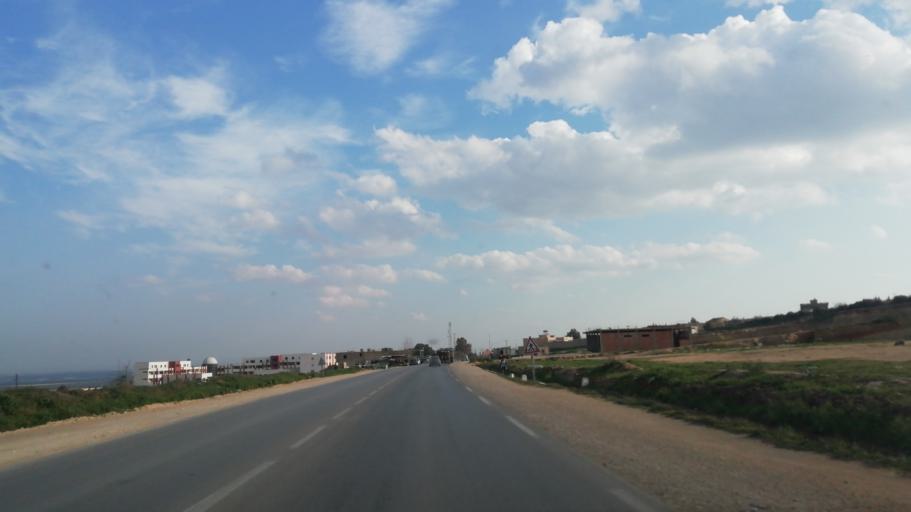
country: DZ
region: Relizane
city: Relizane
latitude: 35.9131
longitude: 0.5013
